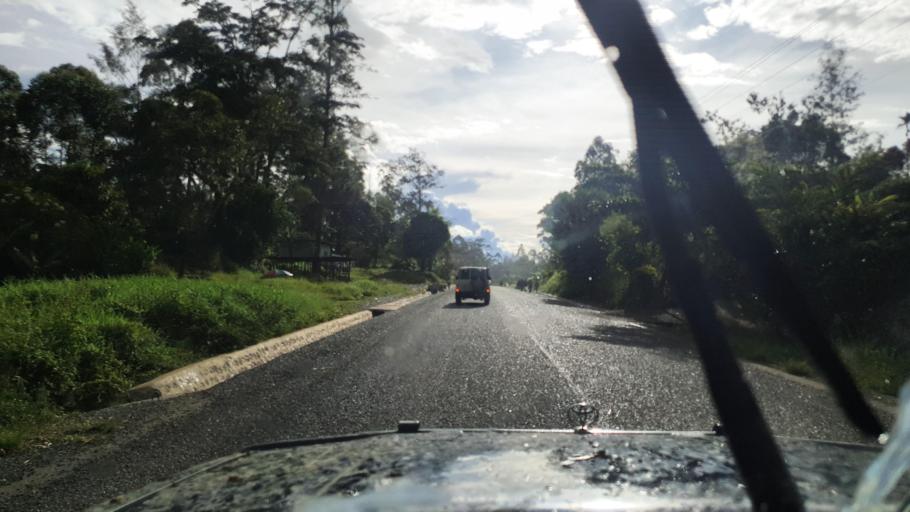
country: PG
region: Jiwaka
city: Minj
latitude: -5.9203
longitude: 144.7738
